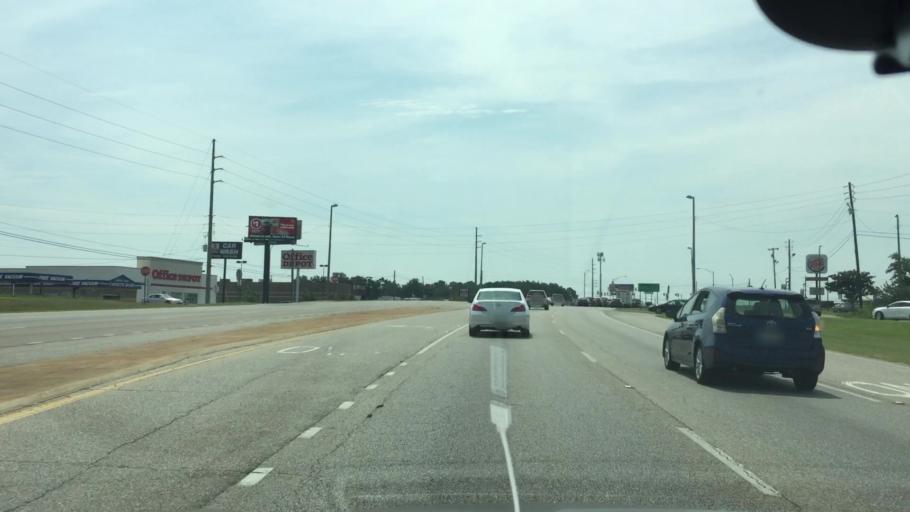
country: US
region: Alabama
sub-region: Coffee County
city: Enterprise
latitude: 31.3253
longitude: -85.8326
